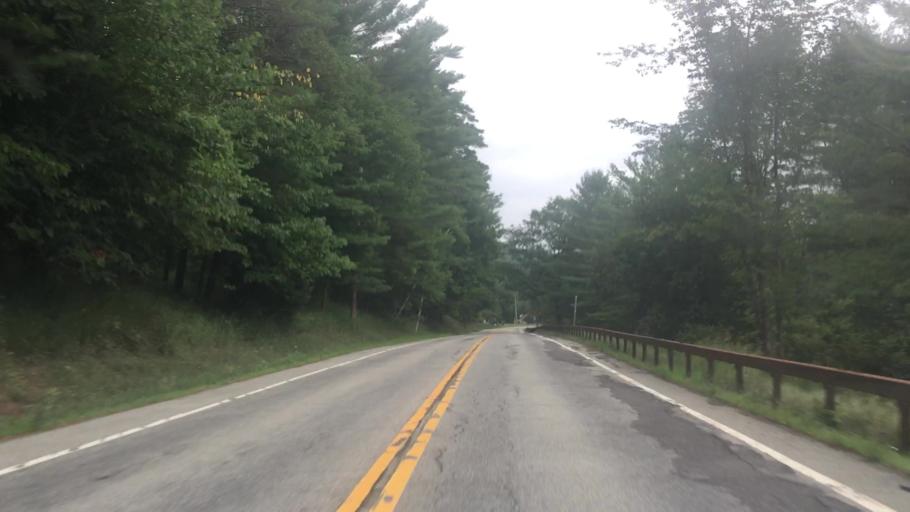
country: US
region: New York
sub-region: Essex County
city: Elizabethtown
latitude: 44.4030
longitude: -73.7049
